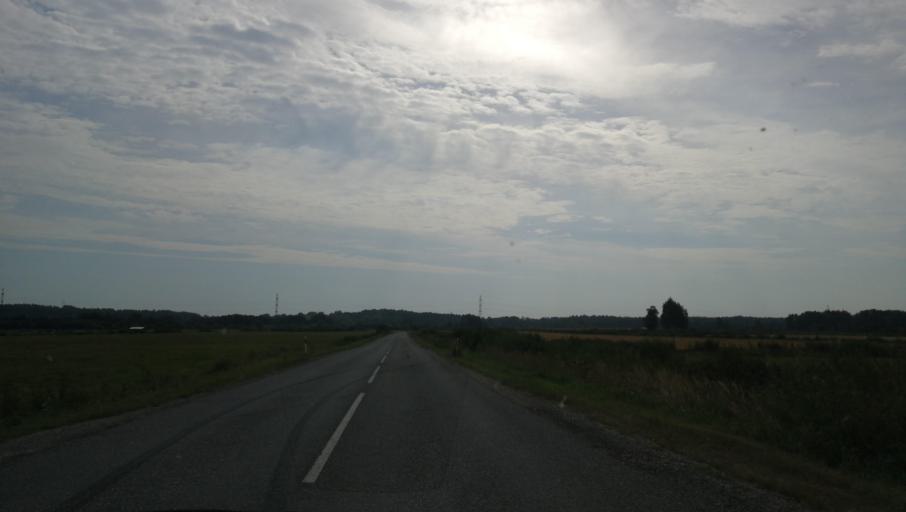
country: LV
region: Alsunga
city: Alsunga
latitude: 56.9866
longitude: 21.5242
